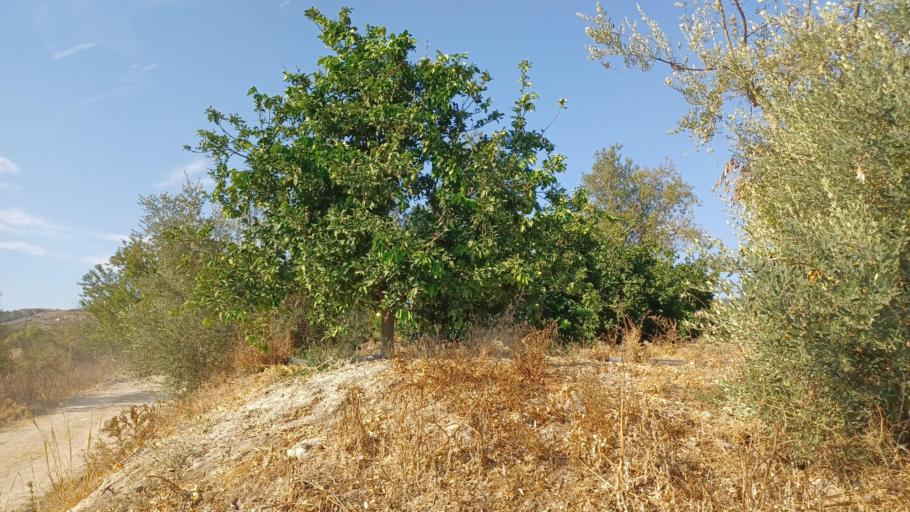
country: CY
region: Pafos
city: Tala
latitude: 34.9151
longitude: 32.4844
